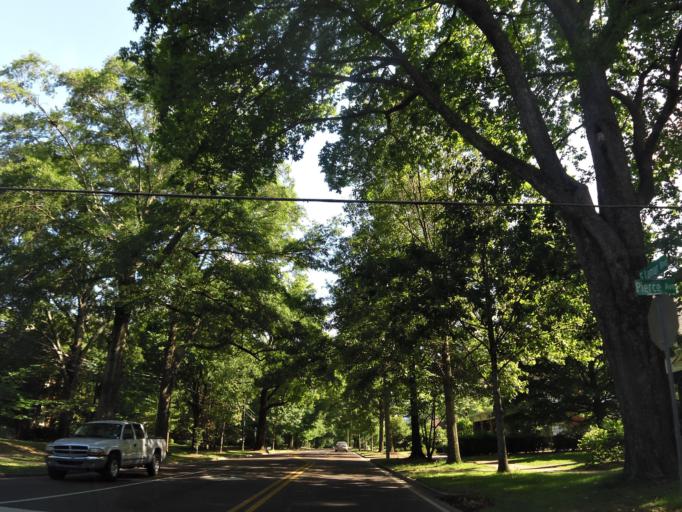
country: US
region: Mississippi
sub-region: Lafayette County
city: Oxford
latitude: 34.3622
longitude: -89.5197
